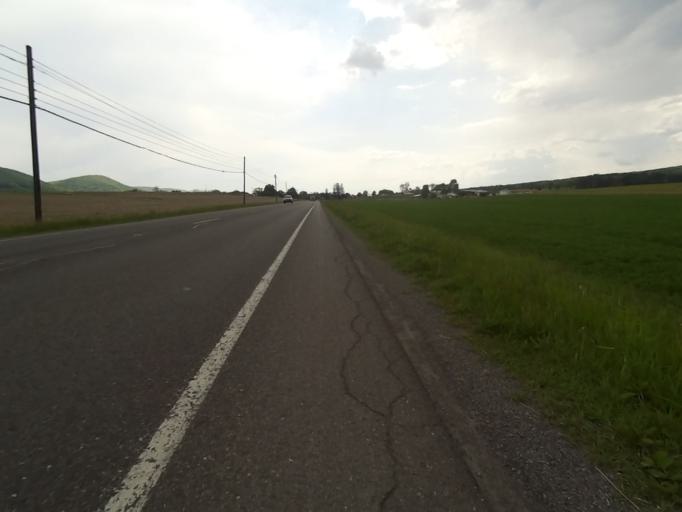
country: US
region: Pennsylvania
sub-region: Centre County
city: Zion
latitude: 40.9507
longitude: -77.6267
